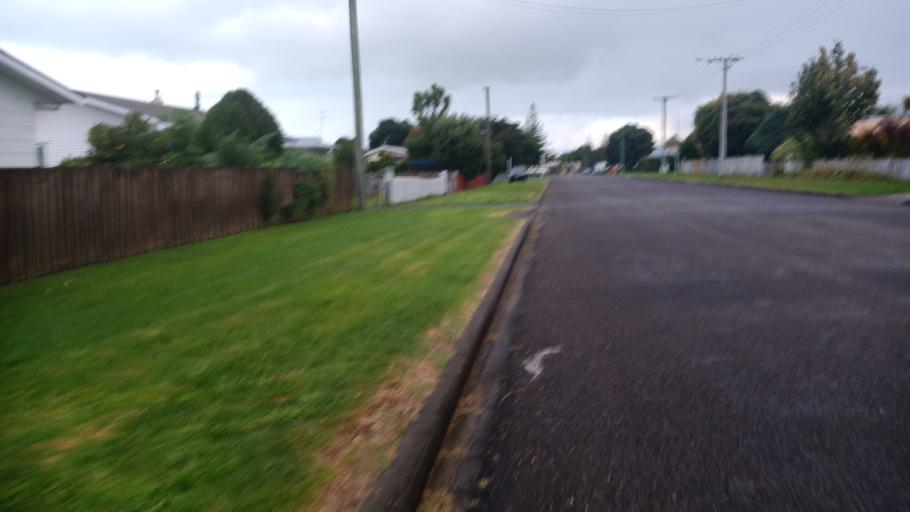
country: NZ
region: Gisborne
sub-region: Gisborne District
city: Gisborne
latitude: -38.6418
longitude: 178.0123
